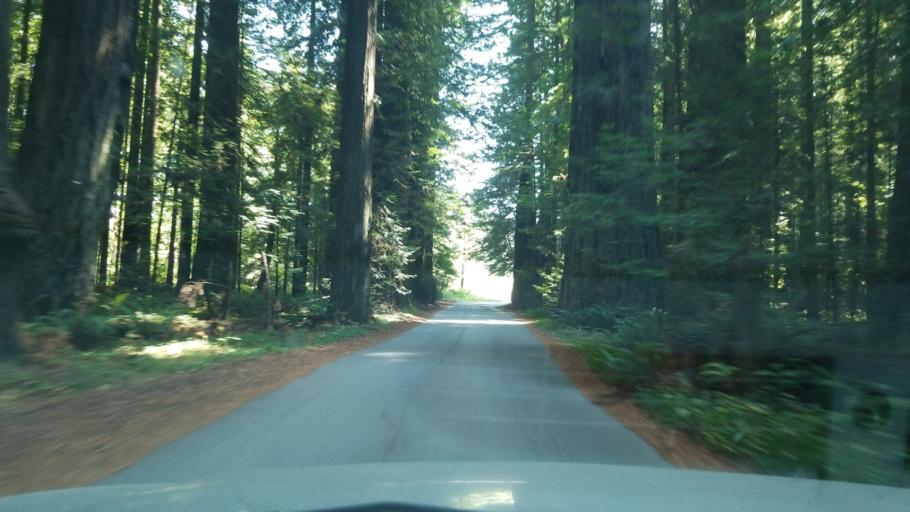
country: US
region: California
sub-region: Humboldt County
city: Rio Dell
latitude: 40.3501
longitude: -123.9198
